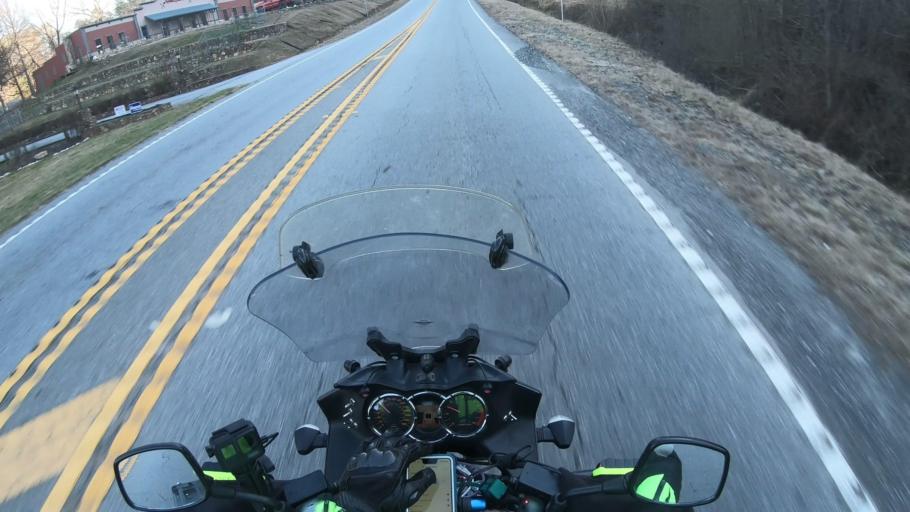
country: US
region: Georgia
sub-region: Lumpkin County
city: Dahlonega
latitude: 34.5630
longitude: -83.9693
